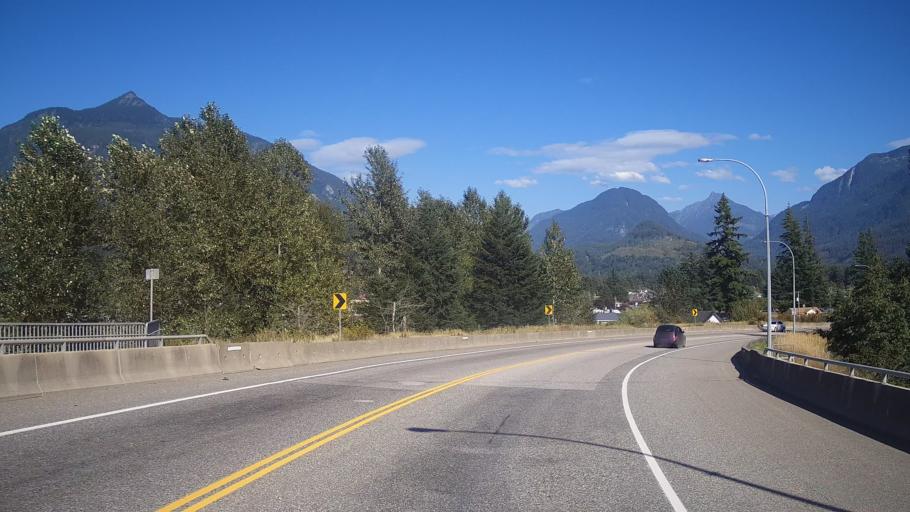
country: CA
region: British Columbia
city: Hope
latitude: 49.3865
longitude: -121.4497
